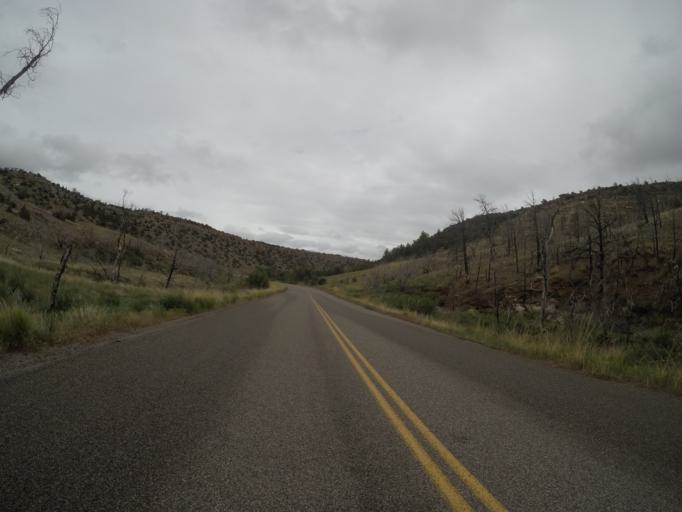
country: US
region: Wyoming
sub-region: Big Horn County
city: Lovell
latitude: 45.1077
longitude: -108.2321
